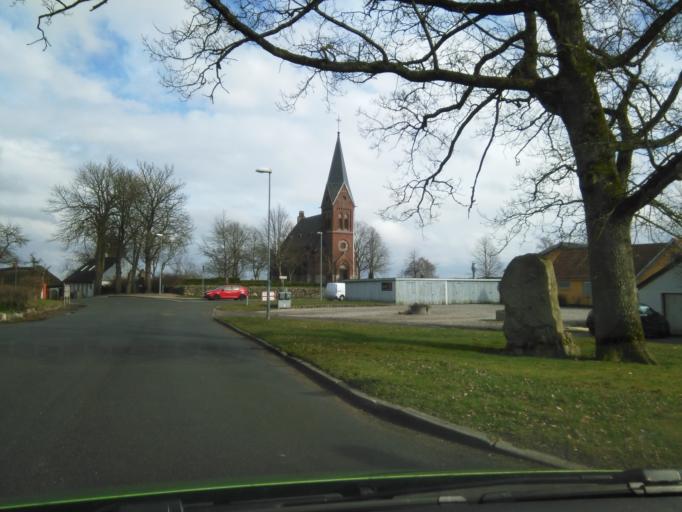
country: DK
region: Central Jutland
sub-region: Skanderborg Kommune
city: Skovby
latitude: 56.1369
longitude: 9.9397
